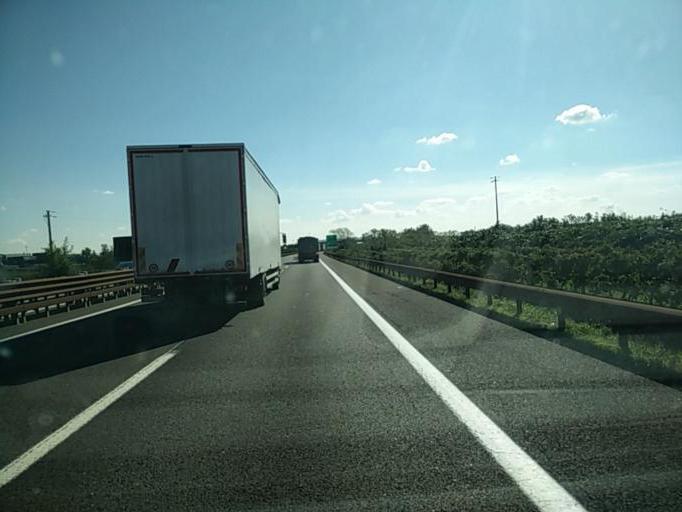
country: IT
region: Veneto
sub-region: Provincia di Verona
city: Caselle
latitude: 45.4204
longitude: 10.9127
